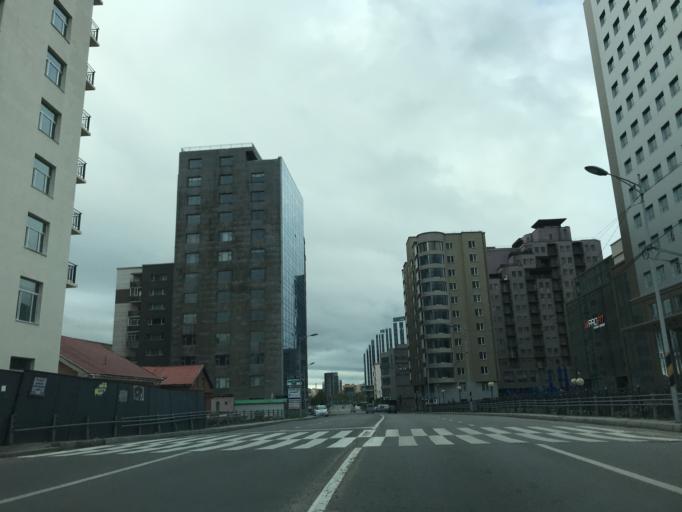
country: MN
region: Ulaanbaatar
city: Ulaanbaatar
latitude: 47.9128
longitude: 106.9300
